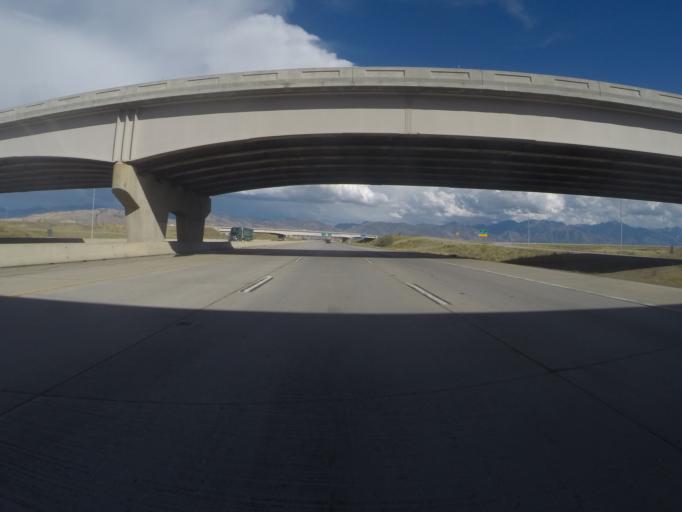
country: US
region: Utah
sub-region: Salt Lake County
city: West Valley City
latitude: 40.7644
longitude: -111.9869
